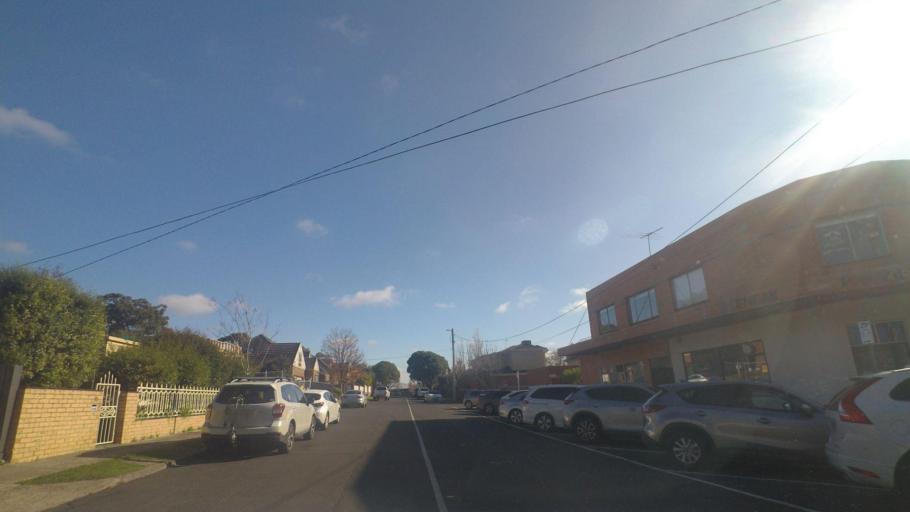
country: AU
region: Victoria
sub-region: Whitehorse
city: Mont Albert North
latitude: -37.8090
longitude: 145.1082
